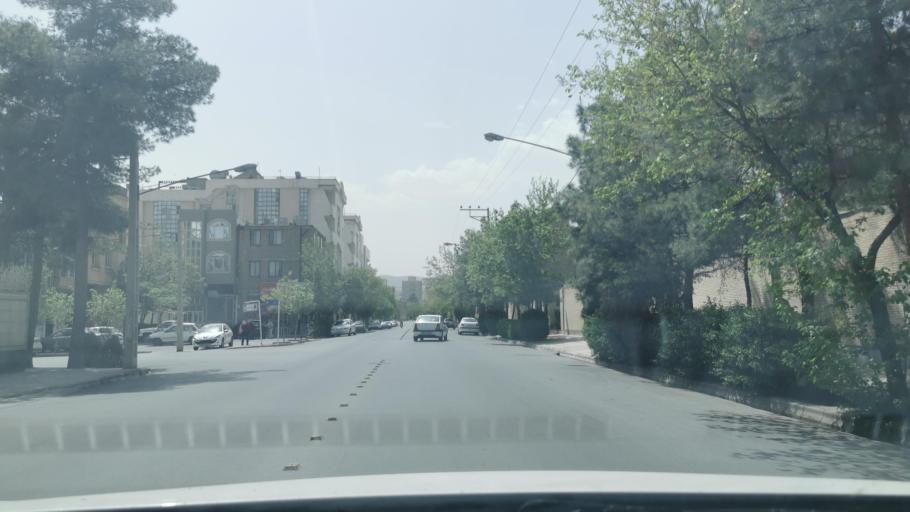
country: IR
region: Razavi Khorasan
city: Mashhad
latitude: 36.3376
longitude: 59.4822
